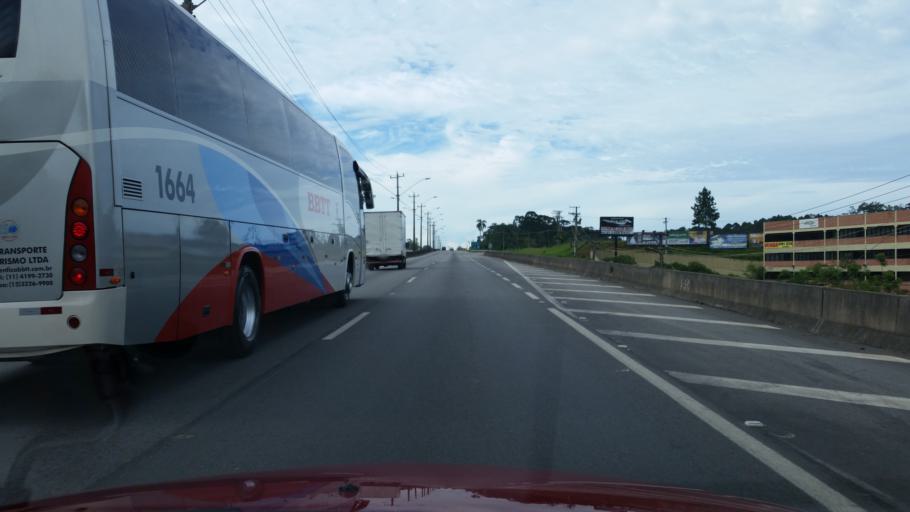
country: BR
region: Sao Paulo
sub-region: Itapecerica Da Serra
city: Itapecerica da Serra
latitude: -23.7276
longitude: -46.8937
